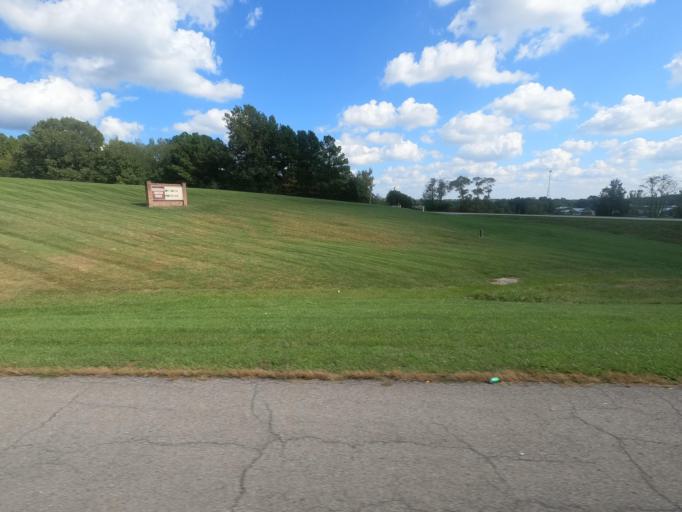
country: US
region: Illinois
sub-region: Johnson County
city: Vienna
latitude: 37.4390
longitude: -88.8930
